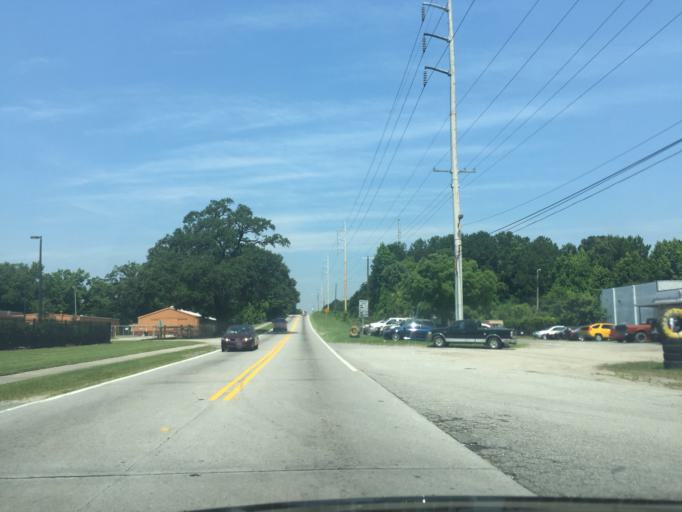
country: US
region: Georgia
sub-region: Chatham County
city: Savannah
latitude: 32.0502
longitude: -81.1224
